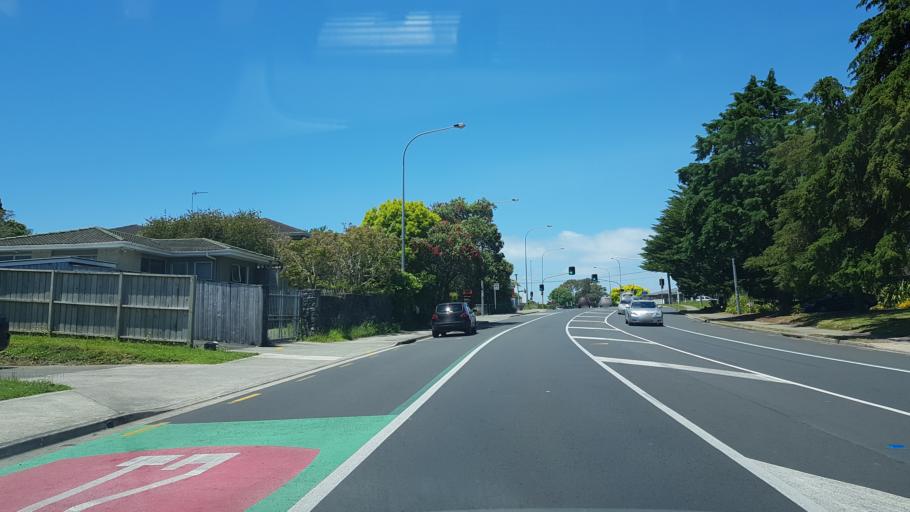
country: NZ
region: Auckland
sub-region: Auckland
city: North Shore
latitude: -36.7954
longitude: 174.7531
